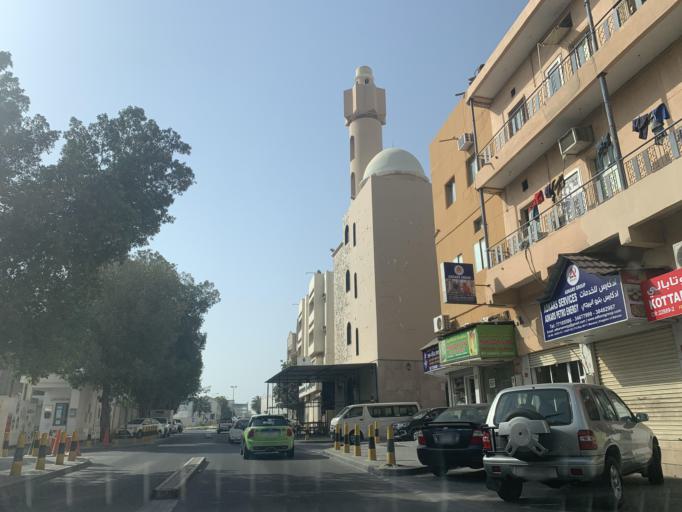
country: BH
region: Manama
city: Manama
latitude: 26.2261
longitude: 50.5770
